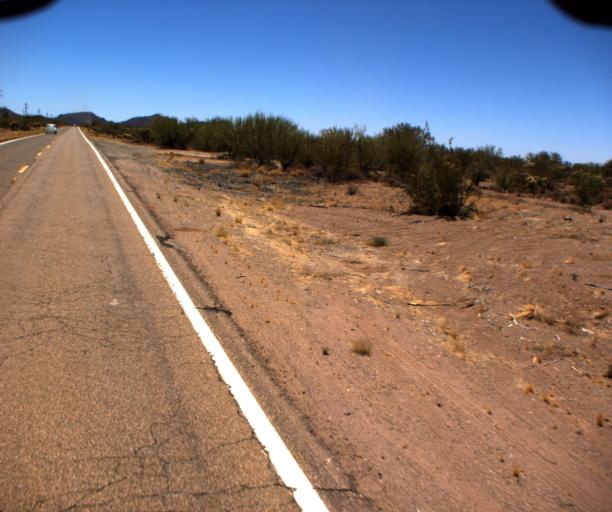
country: US
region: Arizona
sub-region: Pima County
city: Sells
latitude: 32.0009
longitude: -111.9860
